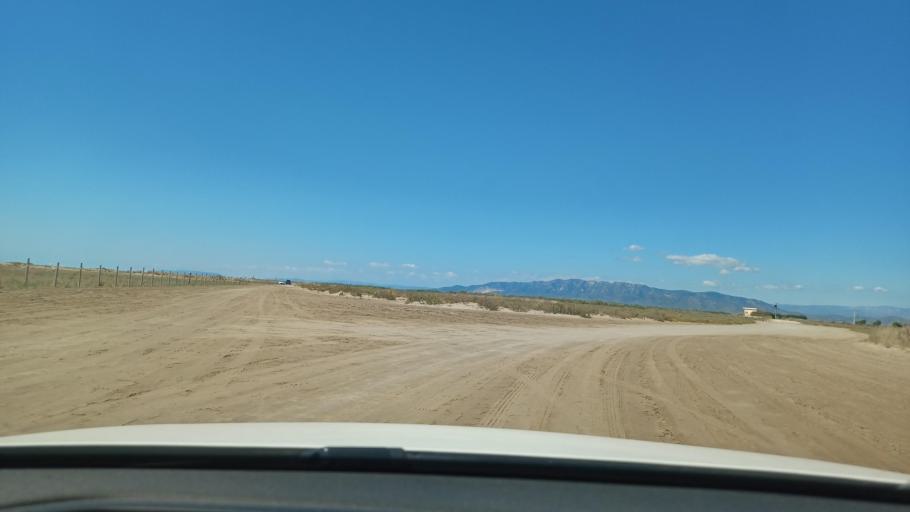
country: ES
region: Catalonia
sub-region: Provincia de Tarragona
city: Deltebre
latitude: 40.6480
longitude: 0.7695
